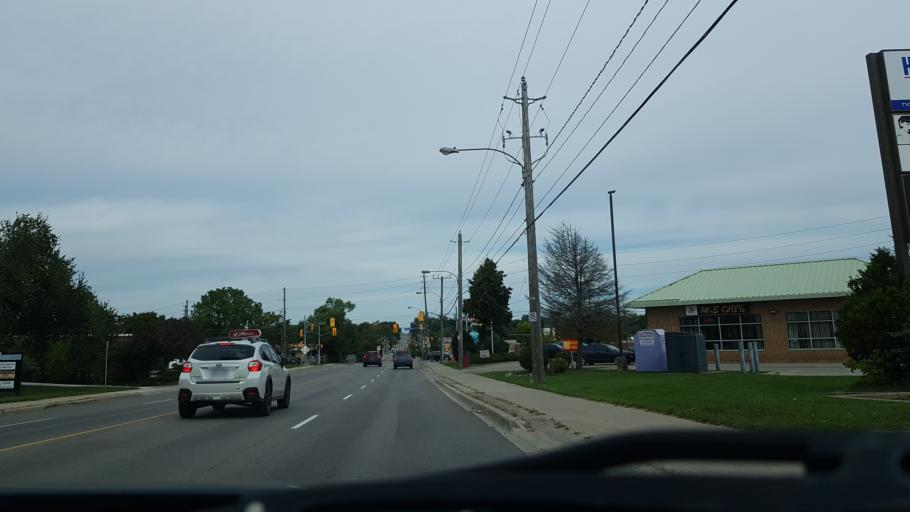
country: CA
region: Ontario
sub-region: Wellington County
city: Guelph
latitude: 43.5560
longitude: -80.2495
